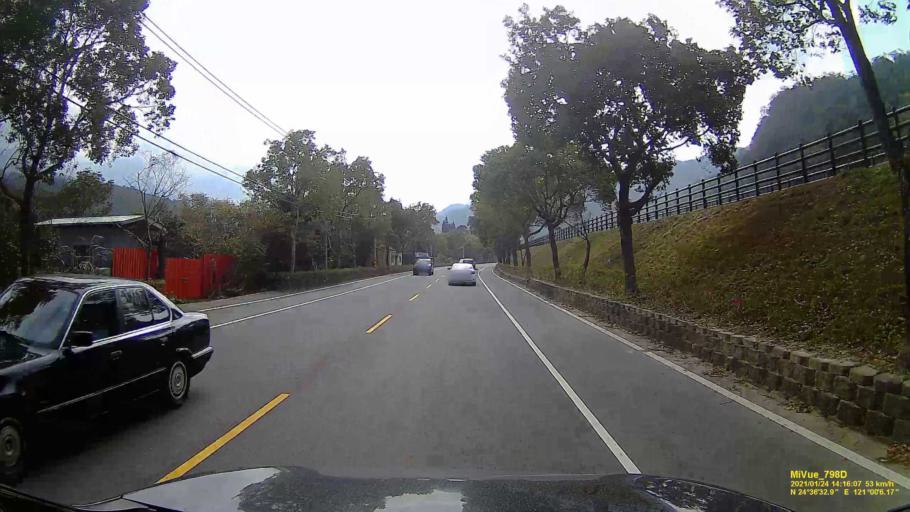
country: TW
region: Taiwan
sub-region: Miaoli
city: Miaoli
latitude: 24.6088
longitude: 121.0015
